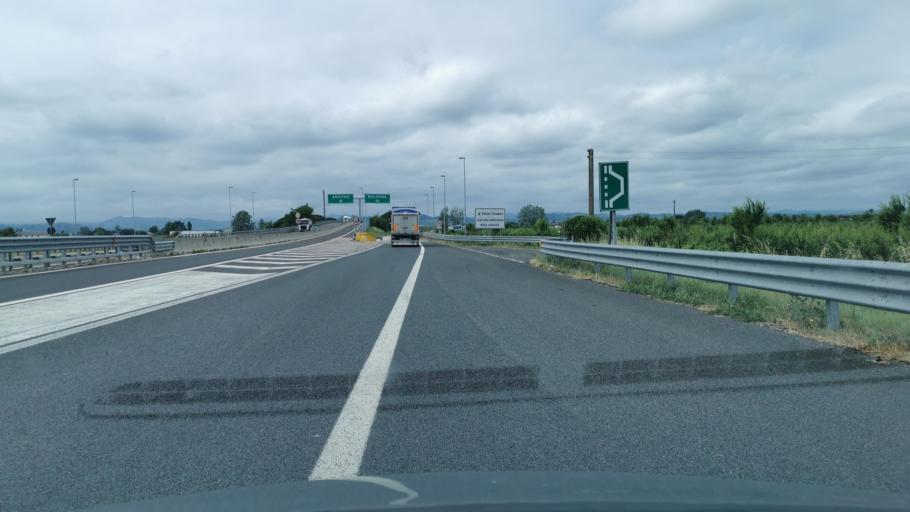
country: IT
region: Emilia-Romagna
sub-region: Provincia di Ravenna
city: Solarolo
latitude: 44.3573
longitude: 11.8195
